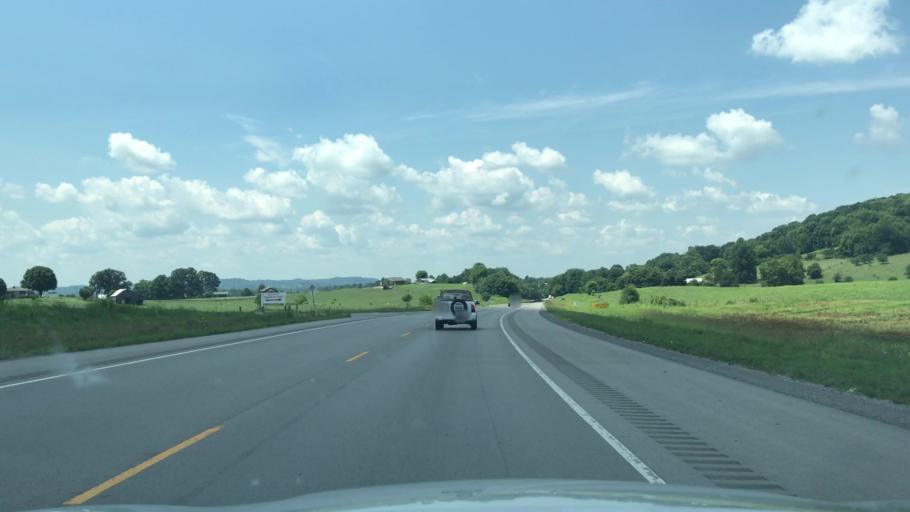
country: US
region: Tennessee
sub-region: Pickett County
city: Byrdstown
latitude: 36.6160
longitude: -85.0924
